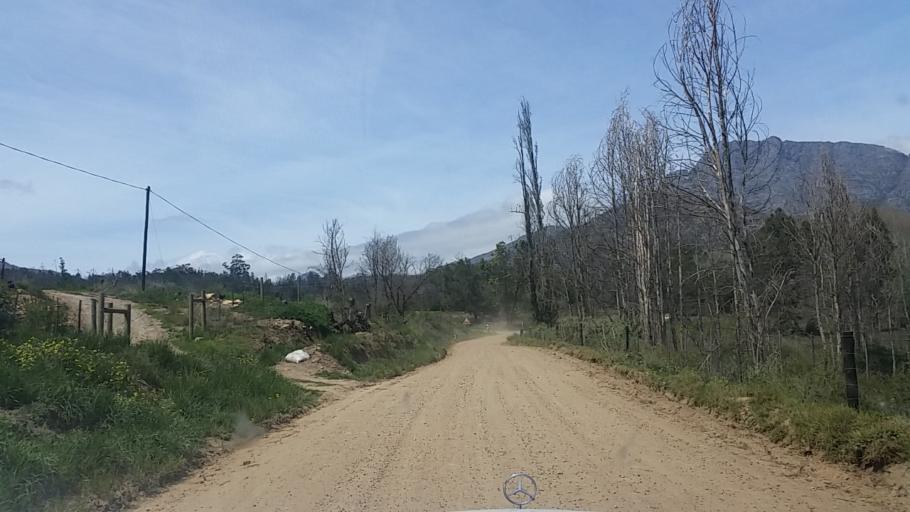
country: ZA
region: Western Cape
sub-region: Eden District Municipality
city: George
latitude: -33.8513
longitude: 22.4503
